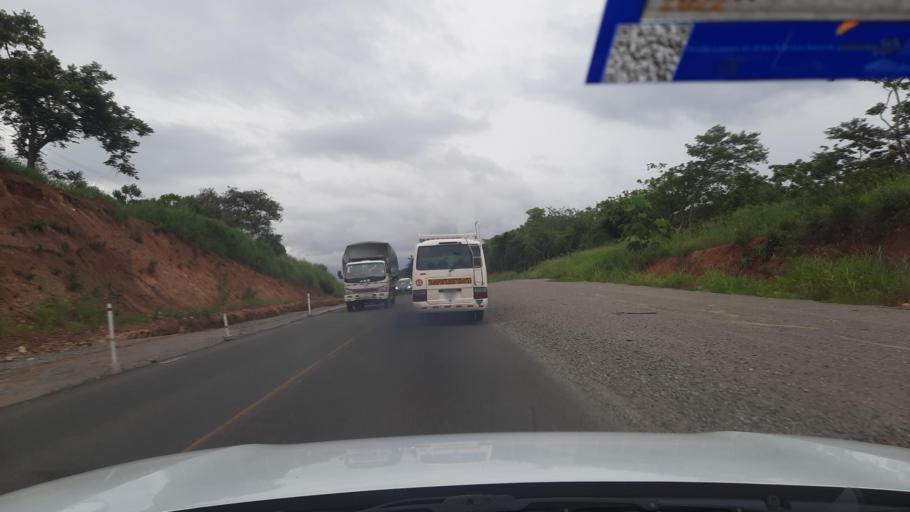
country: CR
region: Puntarenas
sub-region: Canton Central de Puntarenas
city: Puntarenas
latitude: 10.0945
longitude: -84.8558
